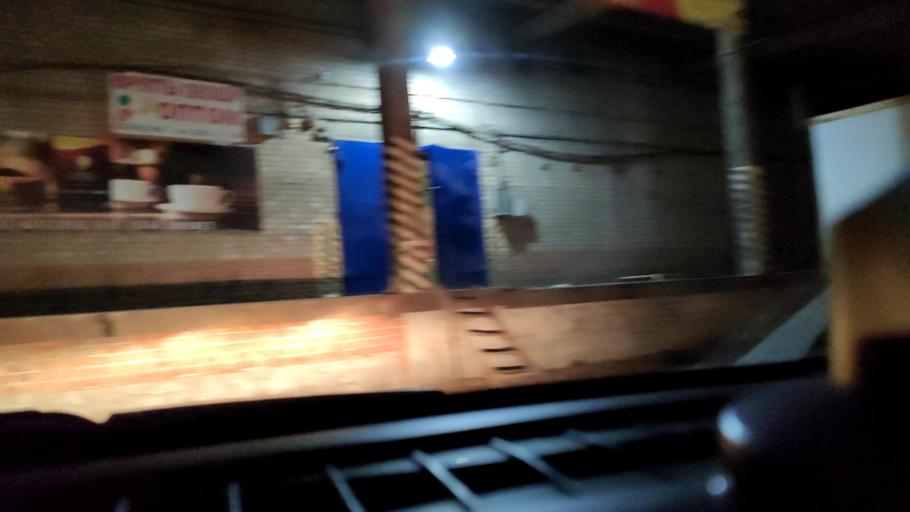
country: RU
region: Perm
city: Froly
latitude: 57.9542
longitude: 56.2589
